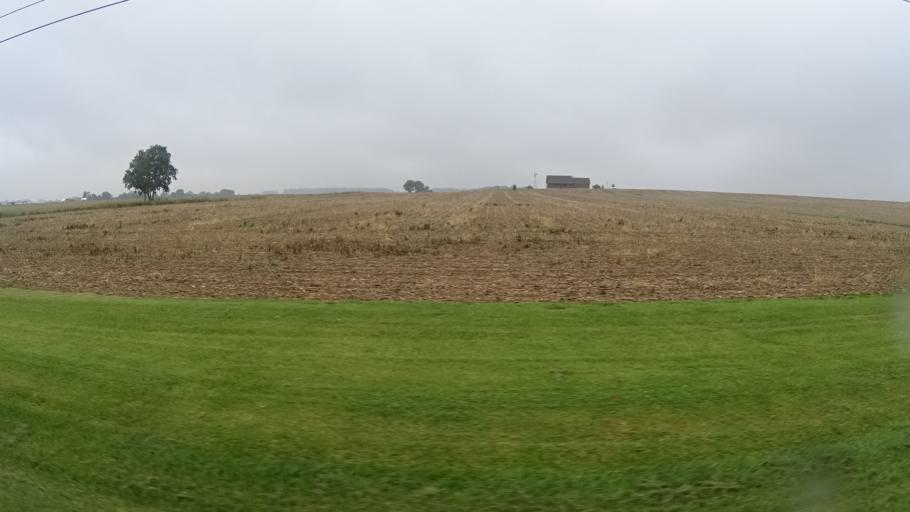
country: US
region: Ohio
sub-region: Huron County
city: Bellevue
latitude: 41.3288
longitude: -82.8431
